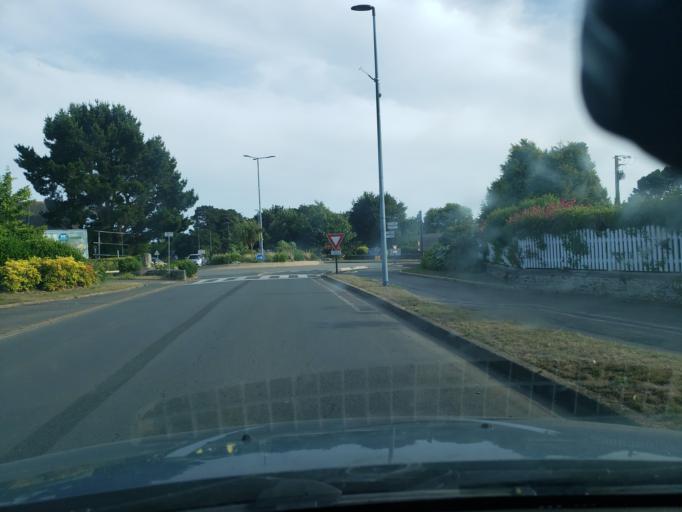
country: FR
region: Brittany
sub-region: Departement du Finistere
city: Plobannalec-Lesconil
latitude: 47.8179
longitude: -4.2296
